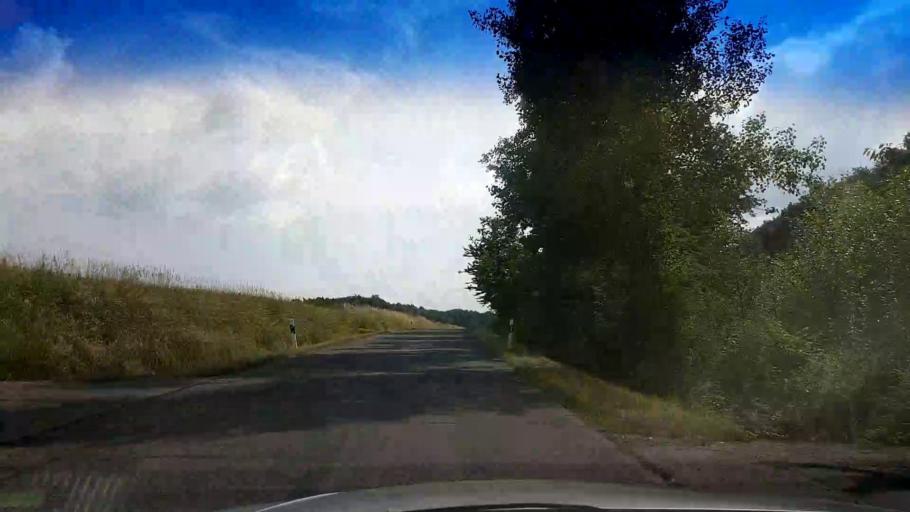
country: DE
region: Bavaria
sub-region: Upper Franconia
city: Priesendorf
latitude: 49.9158
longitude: 10.7431
